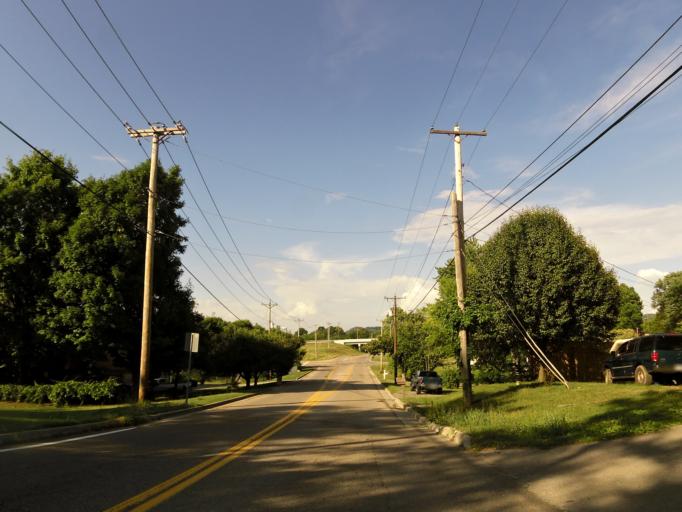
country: US
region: Tennessee
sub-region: Blount County
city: Alcoa
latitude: 35.8251
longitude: -83.9614
